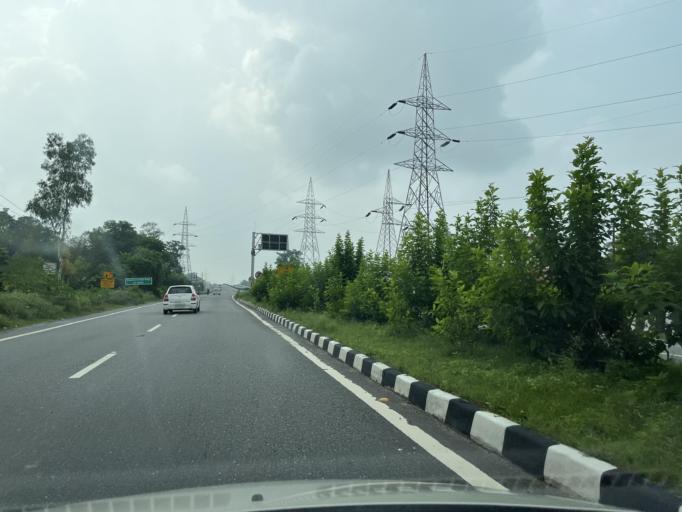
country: IN
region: Uttarakhand
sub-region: Dehradun
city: Doiwala
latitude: 30.1056
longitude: 78.1742
